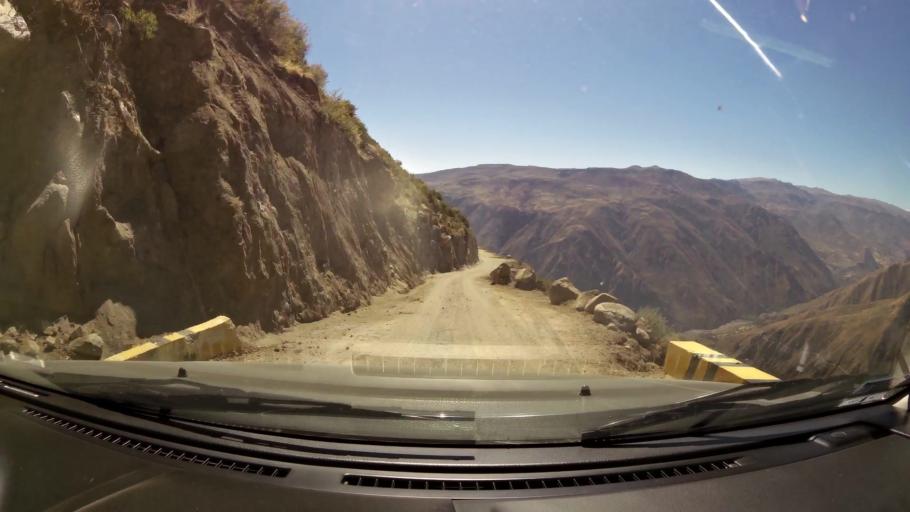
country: PE
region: Huancavelica
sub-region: Huaytara
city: Quito-Arma
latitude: -13.6191
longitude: -75.3512
